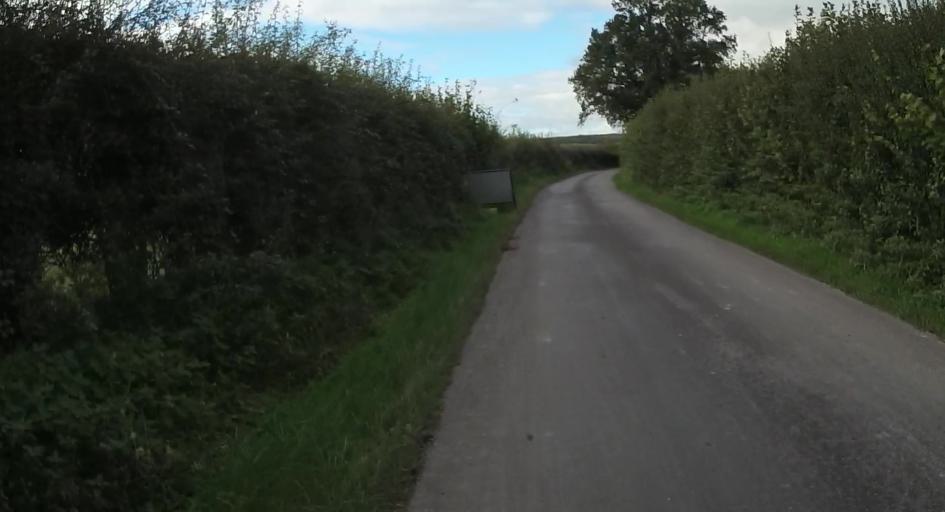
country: GB
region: England
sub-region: Hampshire
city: Alton
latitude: 51.1585
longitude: -0.9250
